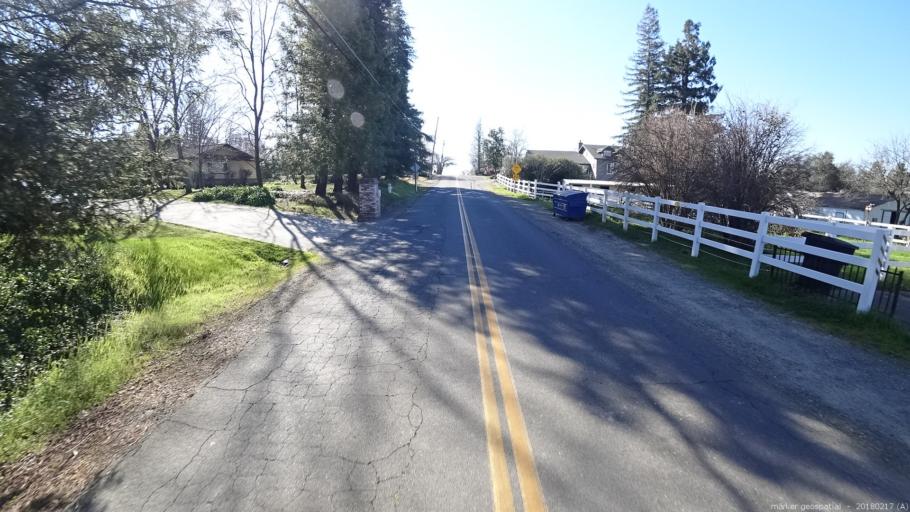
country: US
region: California
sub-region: Sacramento County
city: Orangevale
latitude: 38.7093
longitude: -121.2021
